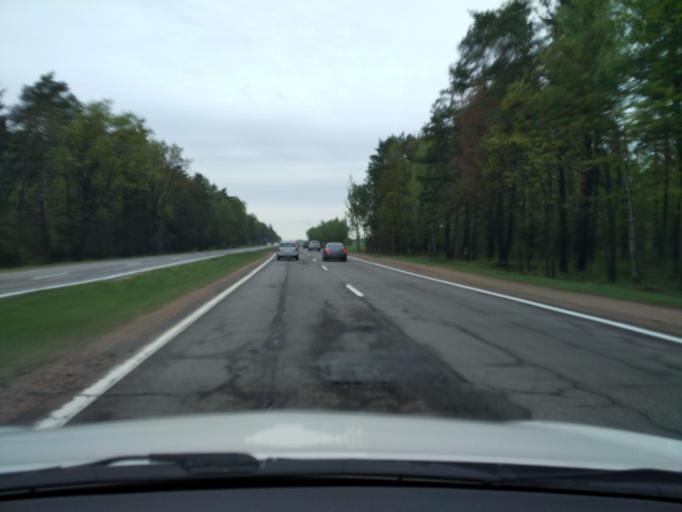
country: BY
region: Minsk
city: Dukora
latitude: 53.6237
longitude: 28.0400
